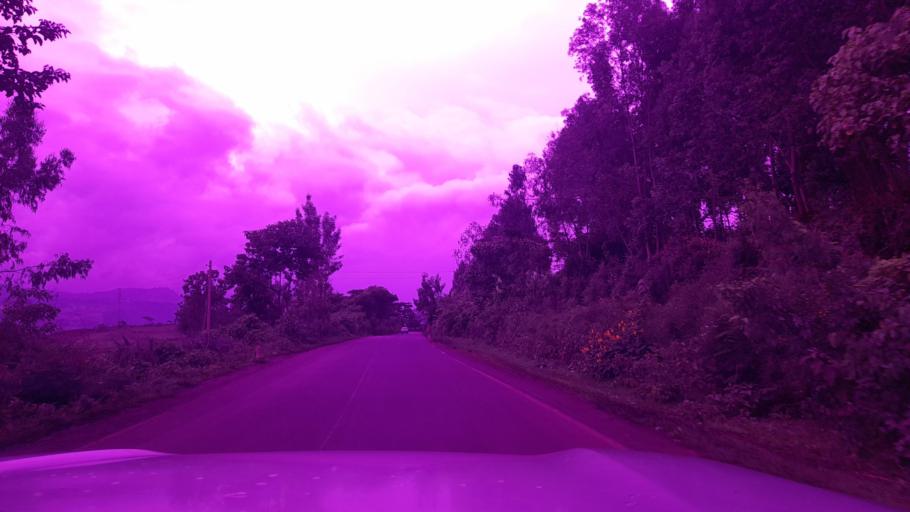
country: ET
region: Oromiya
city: Jima
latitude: 7.9113
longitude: 37.3984
